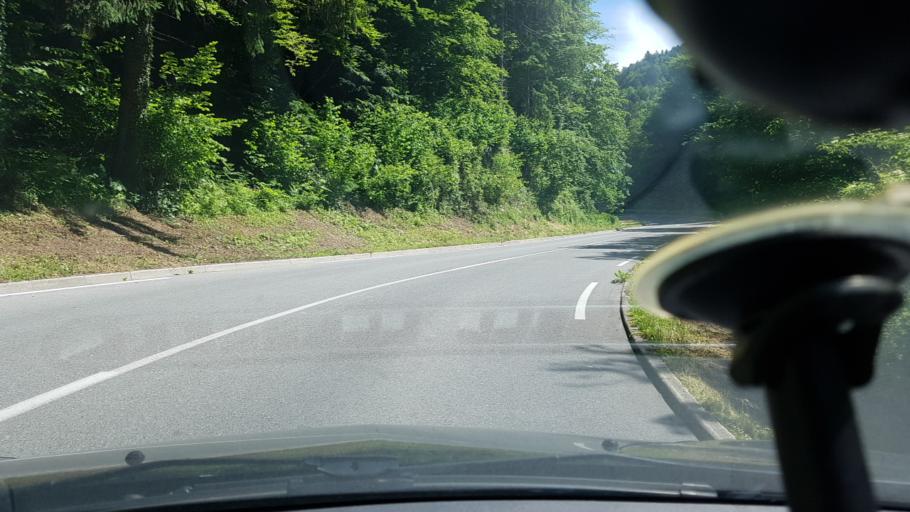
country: SI
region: Zrece
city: Zrece
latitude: 46.3966
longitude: 15.3763
